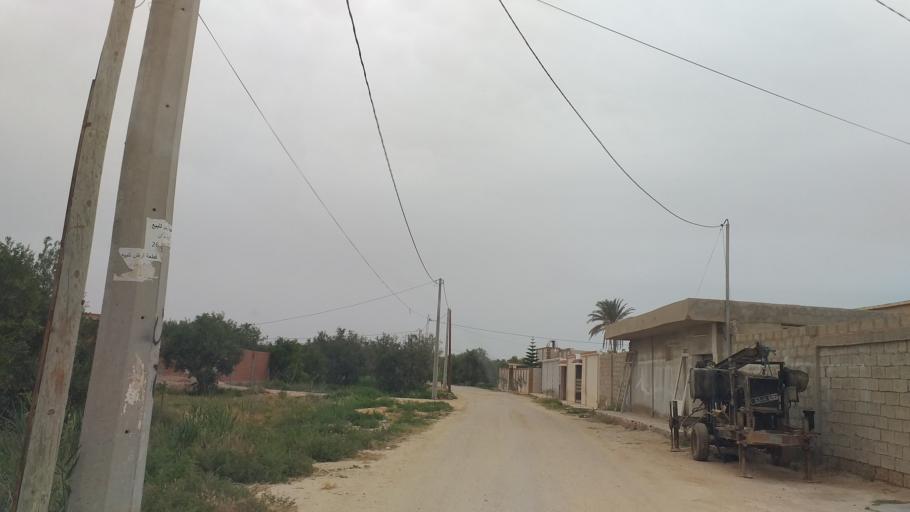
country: TN
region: Qabis
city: Gabes
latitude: 33.9514
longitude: 10.0606
